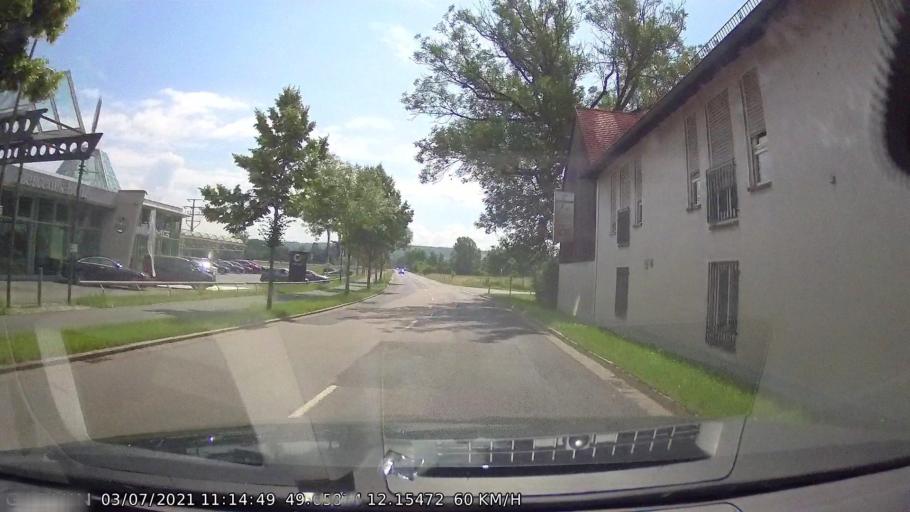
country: DE
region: Bavaria
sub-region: Upper Palatinate
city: Schirmitz
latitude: 49.6587
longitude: 12.1548
